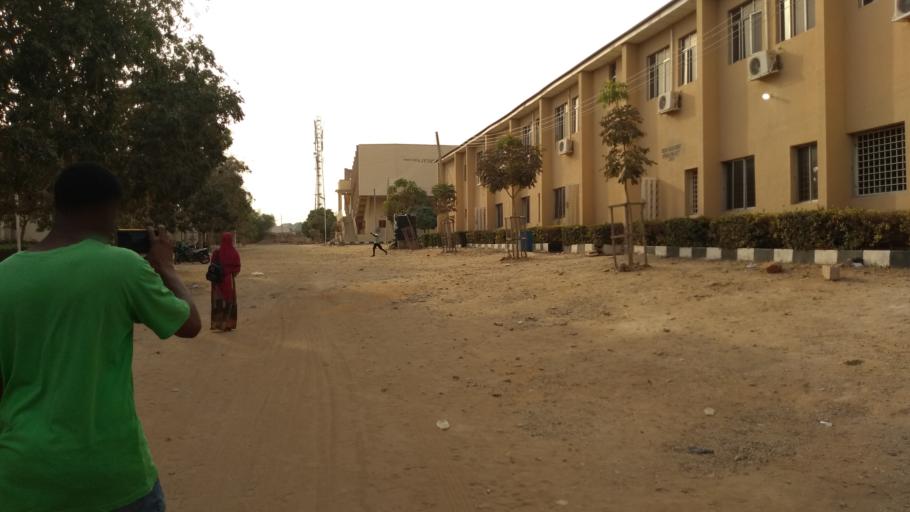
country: NG
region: Gombe
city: Gombe
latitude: 10.3057
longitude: 11.1725
